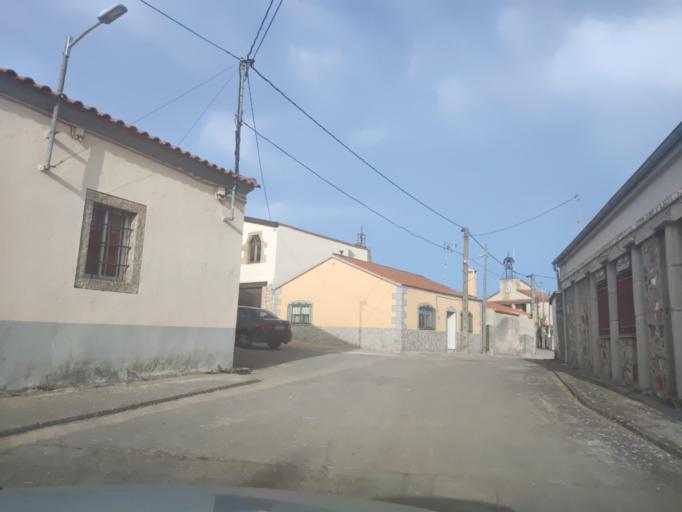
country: ES
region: Castille and Leon
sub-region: Provincia de Salamanca
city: Carpio de Azaba
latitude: 40.5955
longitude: -6.6473
